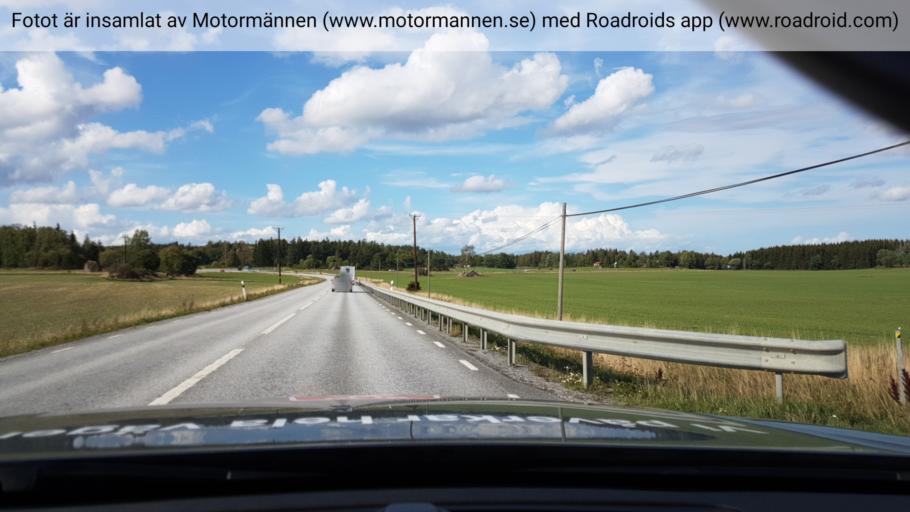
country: SE
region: Uppsala
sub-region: Habo Kommun
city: Balsta
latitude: 59.6273
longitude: 17.6018
